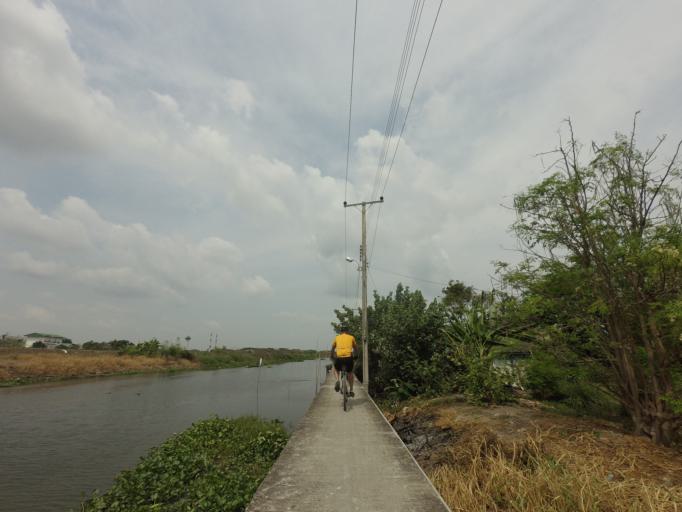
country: TH
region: Bangkok
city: Lat Krabang
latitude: 13.6898
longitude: 100.7721
